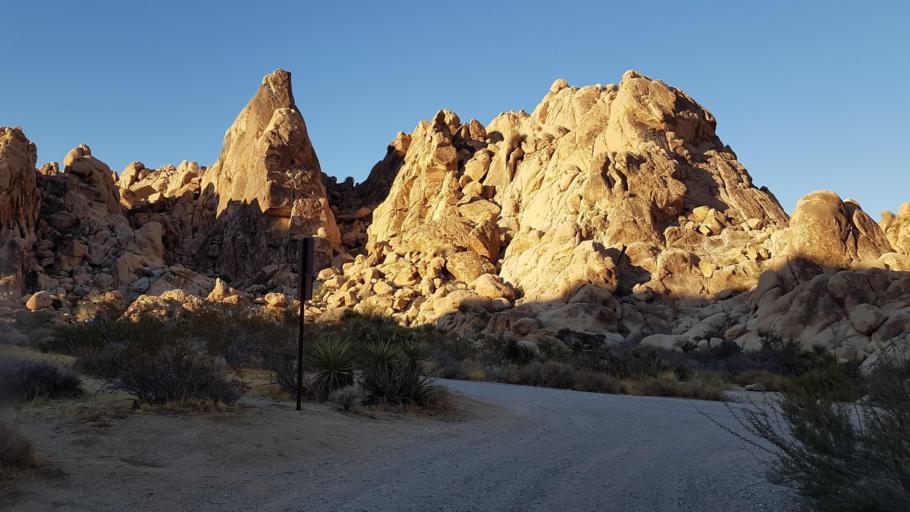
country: US
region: California
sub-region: San Bernardino County
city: Twentynine Palms
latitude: 34.0936
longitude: -116.1644
